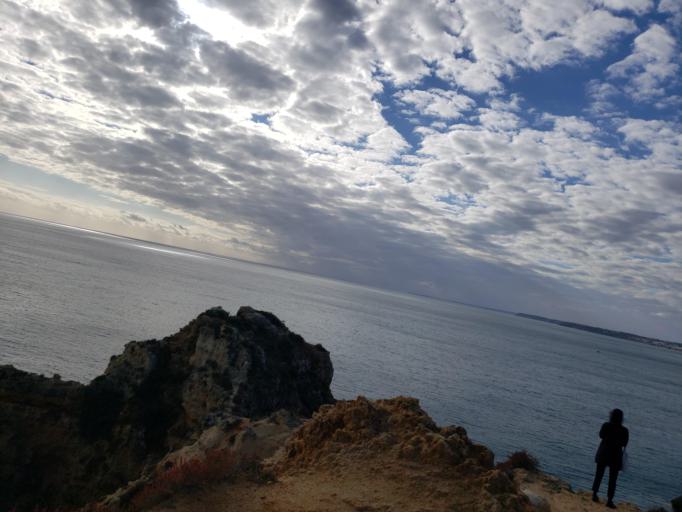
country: PT
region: Faro
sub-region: Lagos
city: Lagos
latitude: 37.0799
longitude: -8.6695
